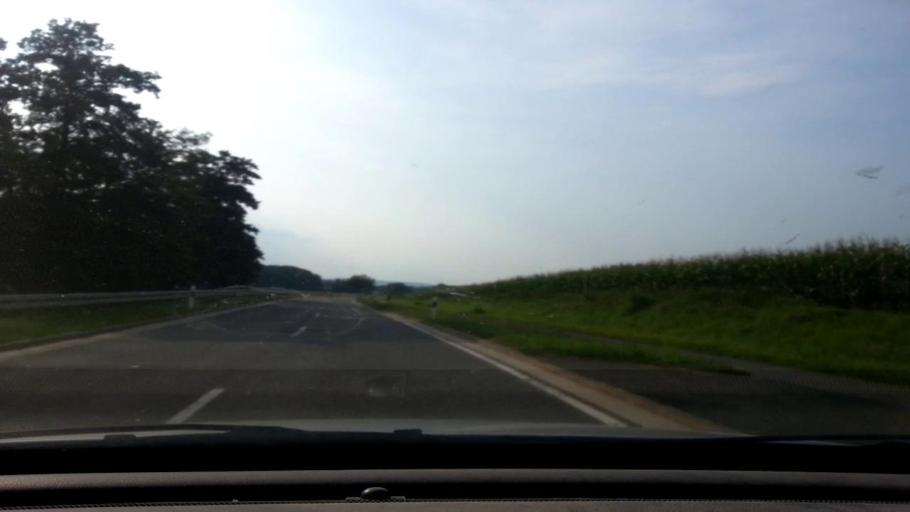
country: DE
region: Bavaria
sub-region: Upper Franconia
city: Litzendorf
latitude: 49.9149
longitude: 10.9860
